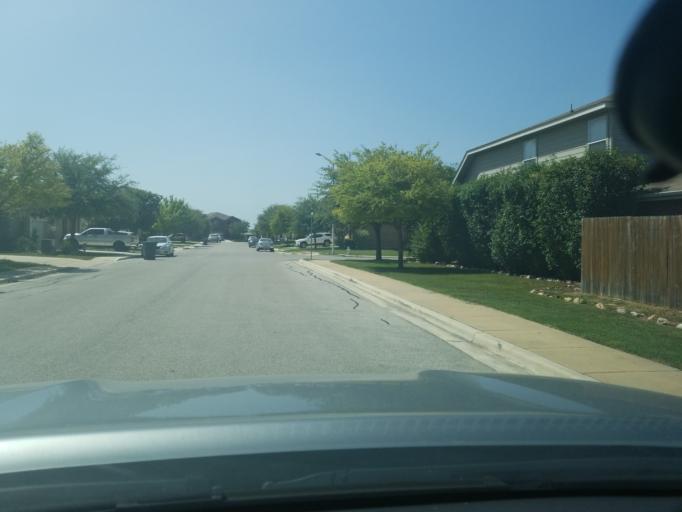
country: US
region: Texas
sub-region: Guadalupe County
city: Lake Dunlap
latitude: 29.6706
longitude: -98.0402
